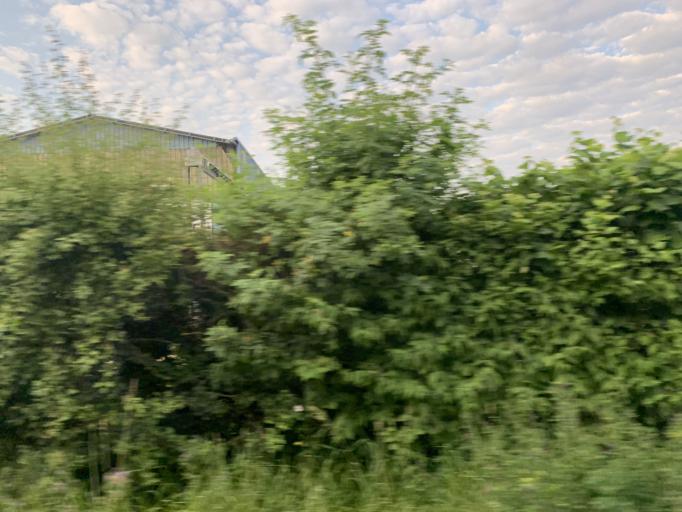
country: FR
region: Rhone-Alpes
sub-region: Departement du Rhone
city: Meyzieu
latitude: 45.7688
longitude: 5.0222
